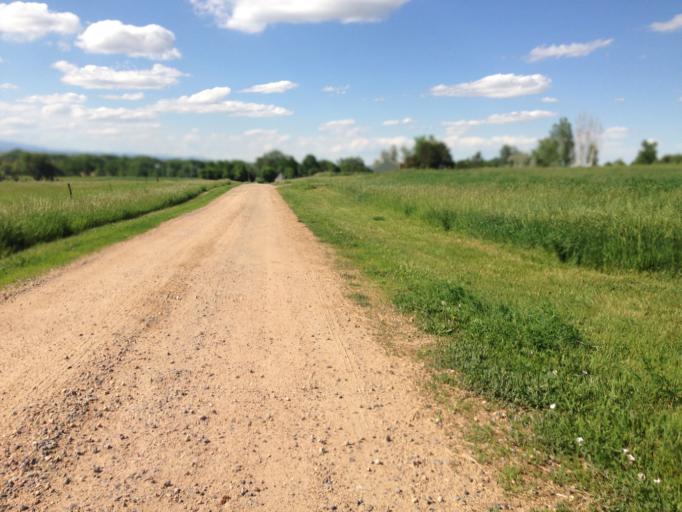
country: US
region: Colorado
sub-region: Boulder County
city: Lafayette
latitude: 40.0115
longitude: -105.1157
